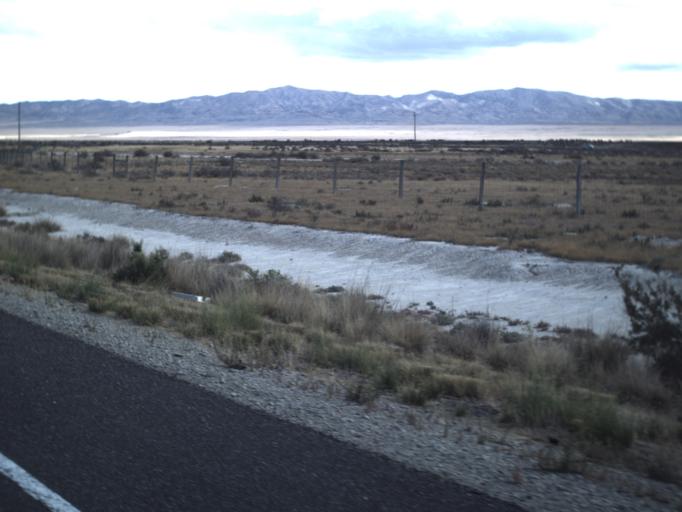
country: US
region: Utah
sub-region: Tooele County
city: Grantsville
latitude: 40.7299
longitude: -113.1192
